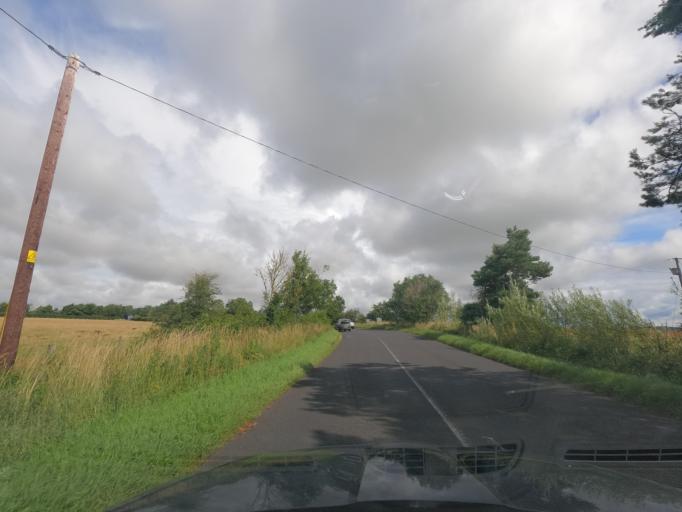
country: GB
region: England
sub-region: Northumberland
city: Lowick
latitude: 55.6245
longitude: -1.9872
